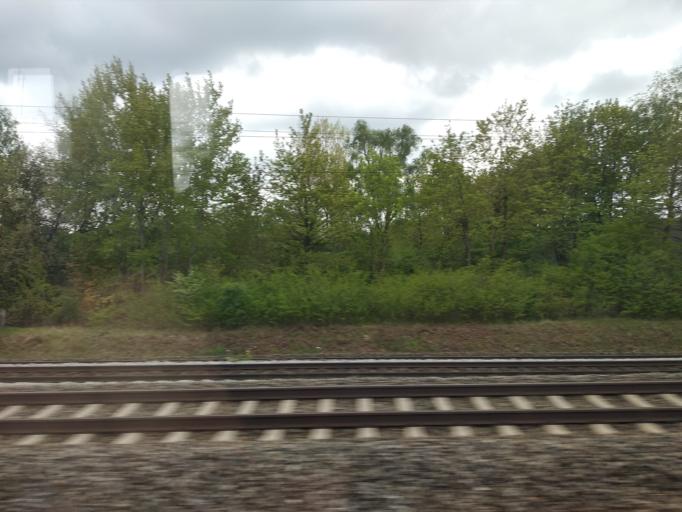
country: DE
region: Bavaria
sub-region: Upper Bavaria
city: Haar
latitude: 48.1199
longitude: 11.6915
